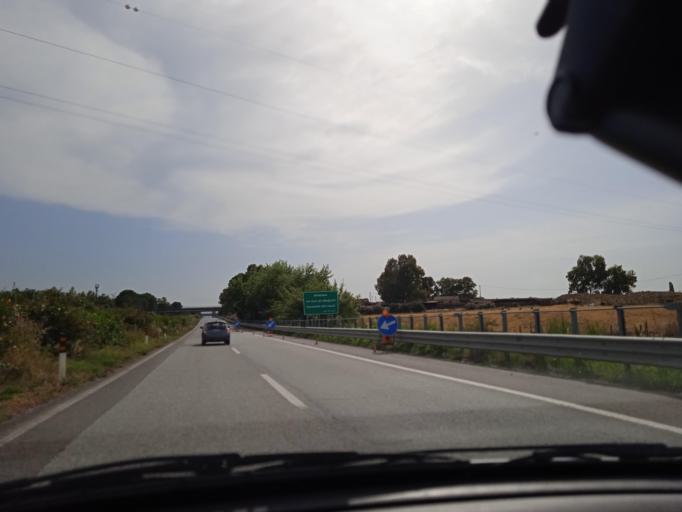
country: IT
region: Sicily
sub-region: Messina
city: San Filippo del Mela
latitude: 38.1895
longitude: 15.2682
